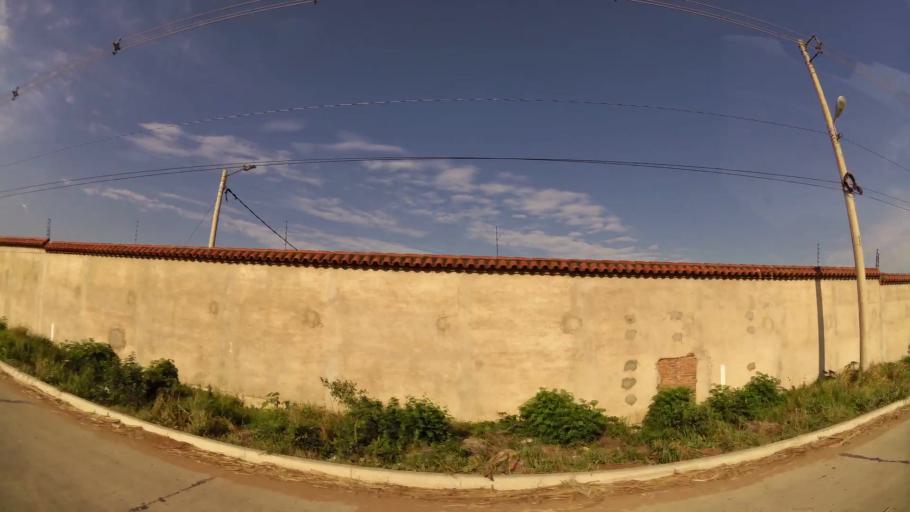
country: BO
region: Santa Cruz
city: Santa Cruz de la Sierra
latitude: -17.6806
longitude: -63.1527
